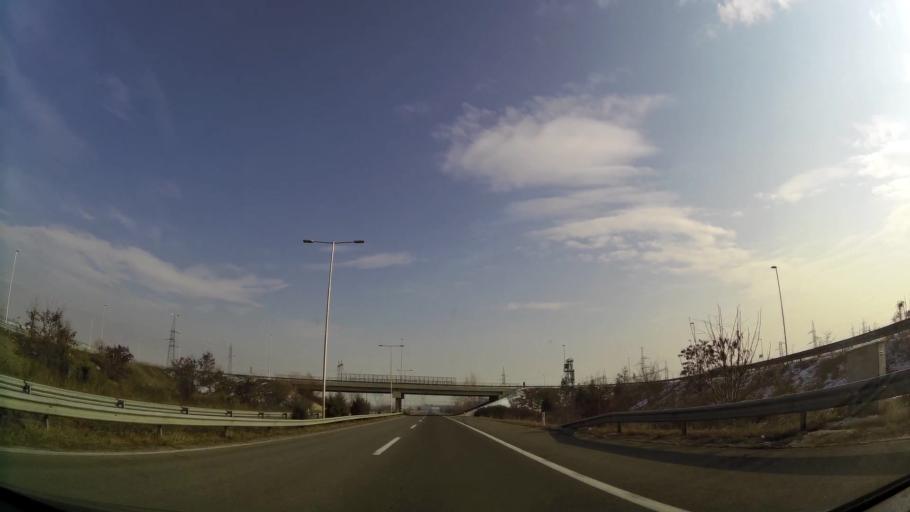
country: MK
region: Butel
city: Butel
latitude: 42.0410
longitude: 21.4539
